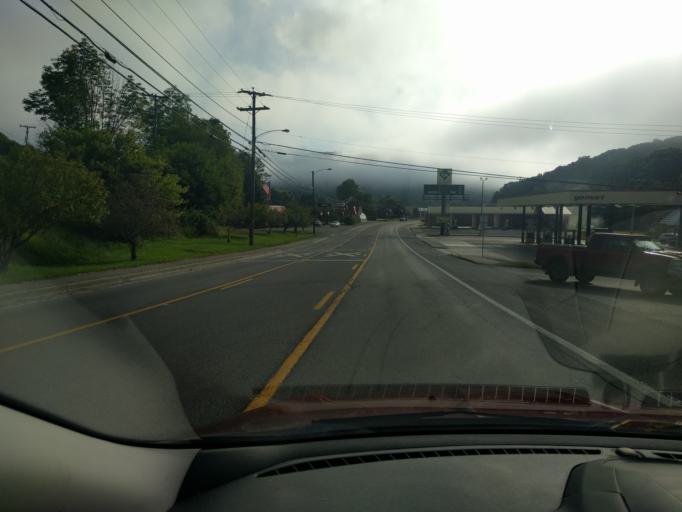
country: US
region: West Virginia
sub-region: Greenbrier County
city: Rainelle
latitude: 37.9683
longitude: -80.7722
